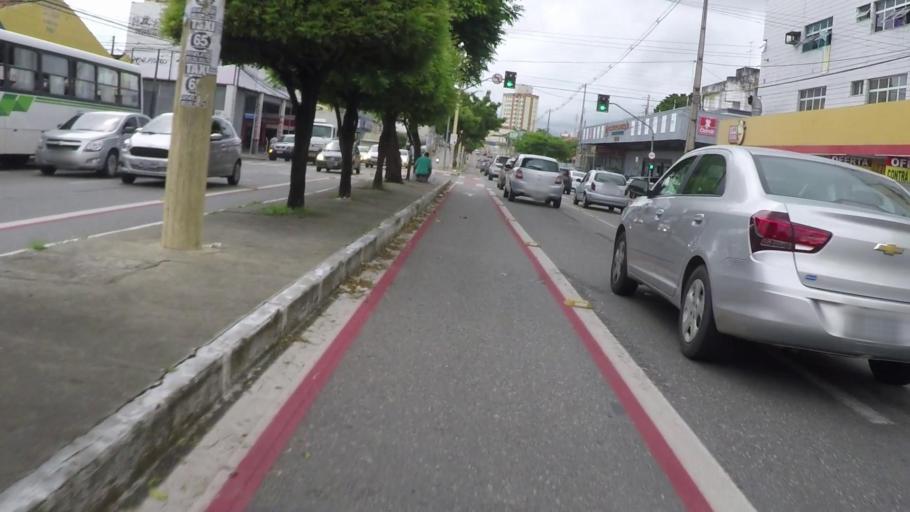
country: BR
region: Ceara
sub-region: Fortaleza
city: Fortaleza
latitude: -3.7377
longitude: -38.5276
